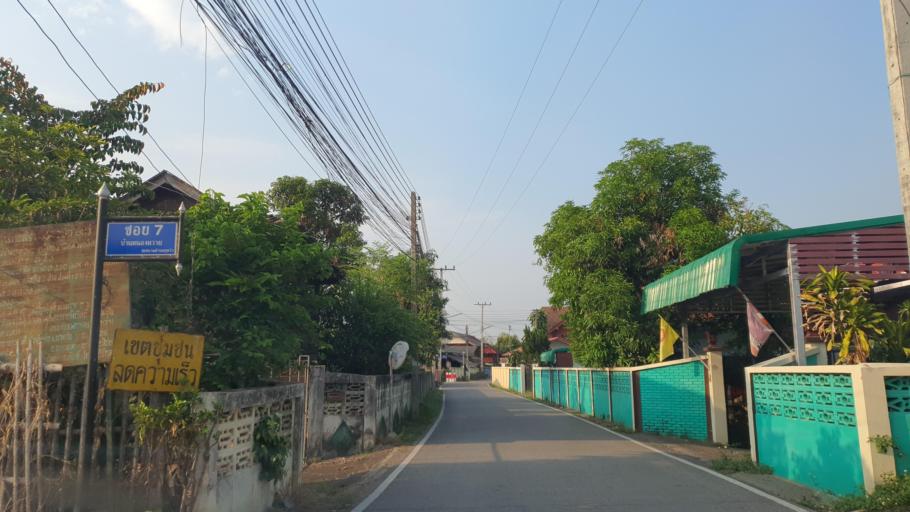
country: TH
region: Chiang Mai
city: San Pa Tong
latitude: 18.6403
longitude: 98.8710
